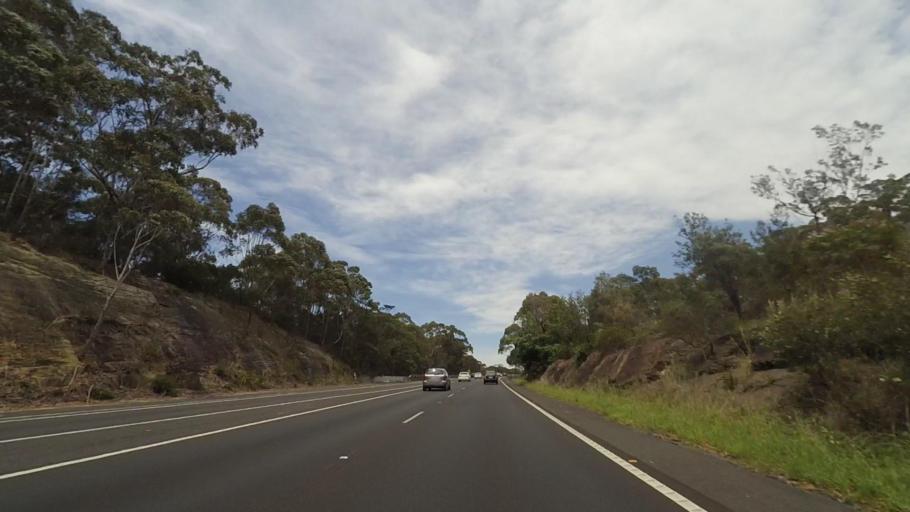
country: AU
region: New South Wales
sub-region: Wollongong
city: Helensburgh
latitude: -34.2045
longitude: 150.9647
